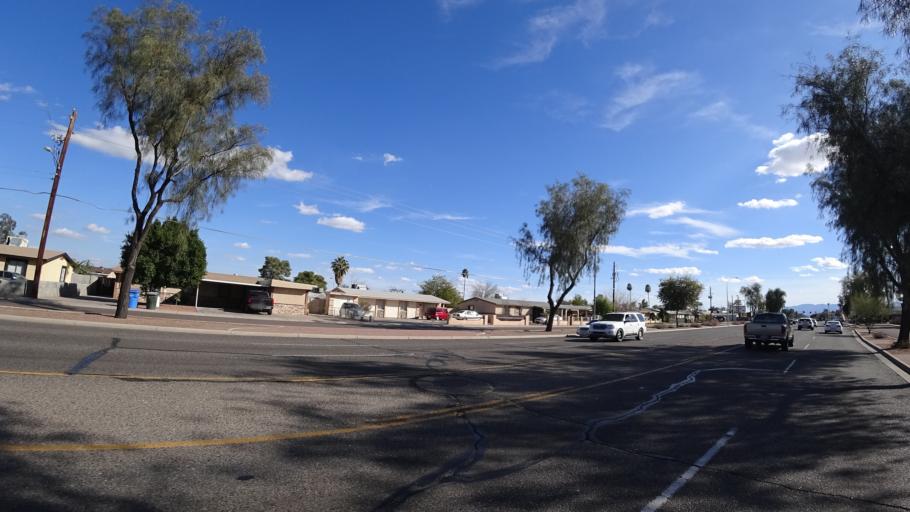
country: US
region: Arizona
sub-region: Maricopa County
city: Glendale
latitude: 33.4976
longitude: -112.2206
